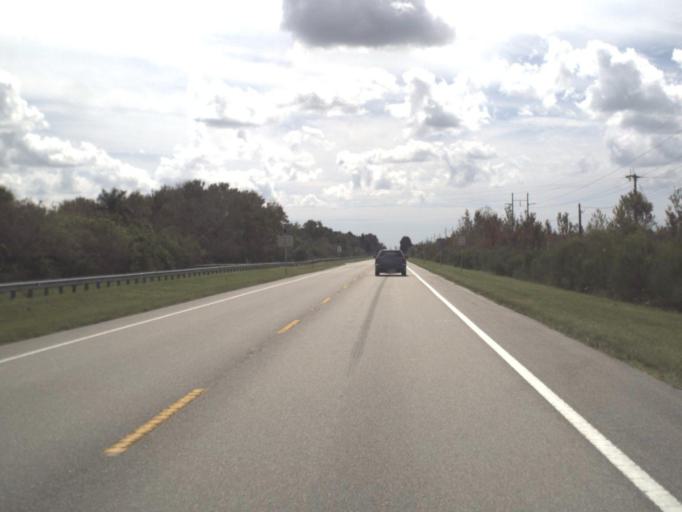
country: US
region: Florida
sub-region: Collier County
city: Lely Resort
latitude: 25.9662
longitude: -81.3532
